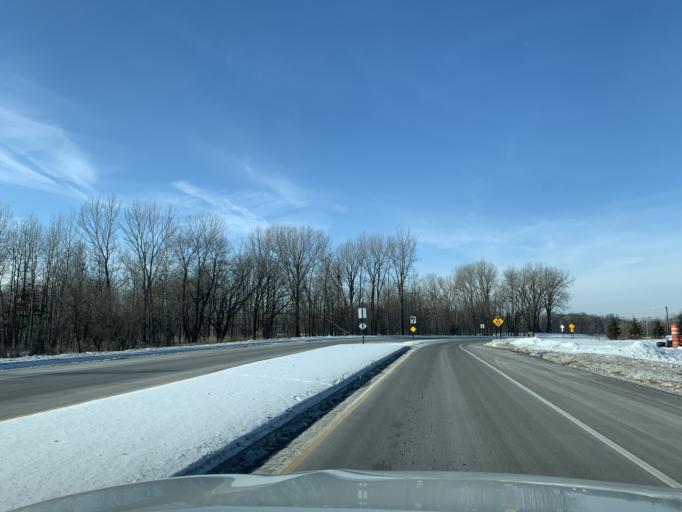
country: US
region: Minnesota
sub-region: Anoka County
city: Columbus
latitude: 45.2485
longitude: -93.0285
